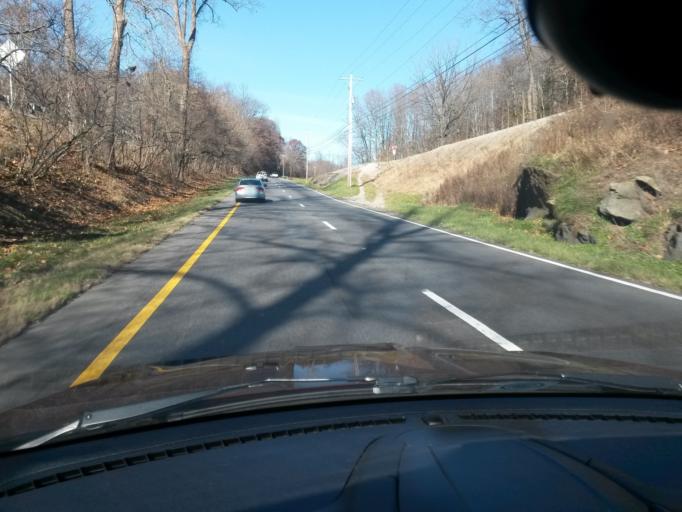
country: US
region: Virginia
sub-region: Roanoke County
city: Narrows
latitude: 37.1358
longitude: -79.9727
